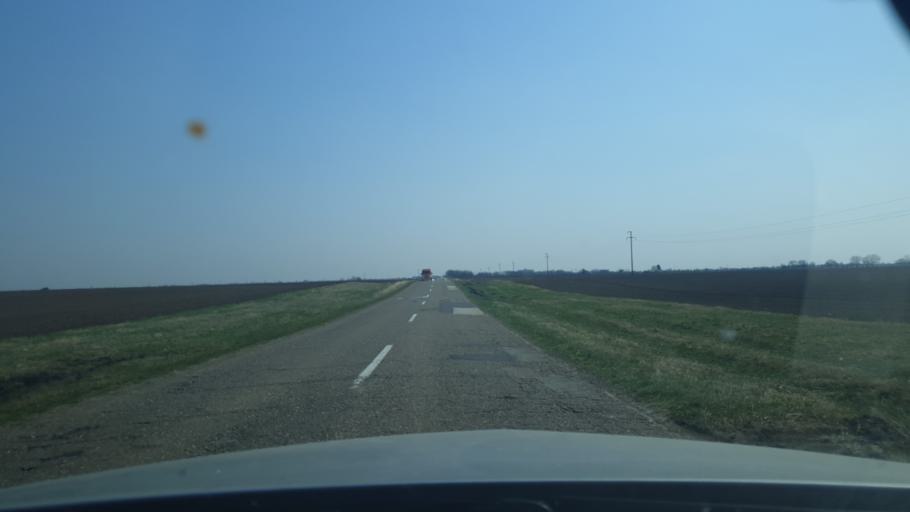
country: RS
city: Sasinci
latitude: 45.0280
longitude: 19.7560
